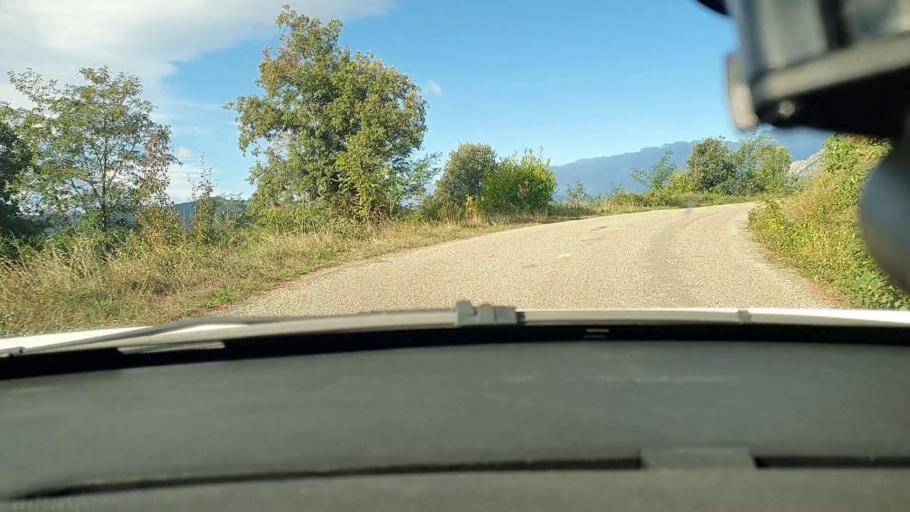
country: FR
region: Languedoc-Roussillon
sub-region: Departement du Gard
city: Besseges
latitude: 44.3370
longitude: 3.9914
